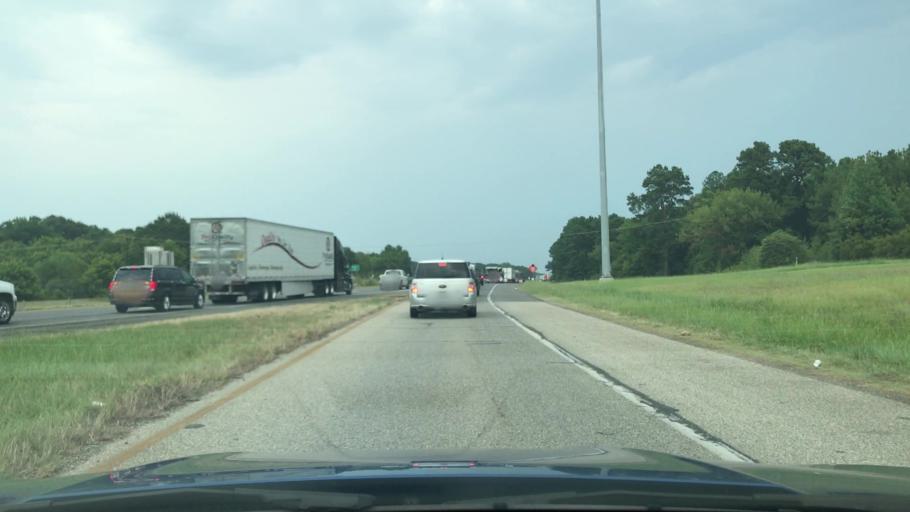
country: US
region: Texas
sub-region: Harrison County
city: Waskom
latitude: 32.4657
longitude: -94.0527
